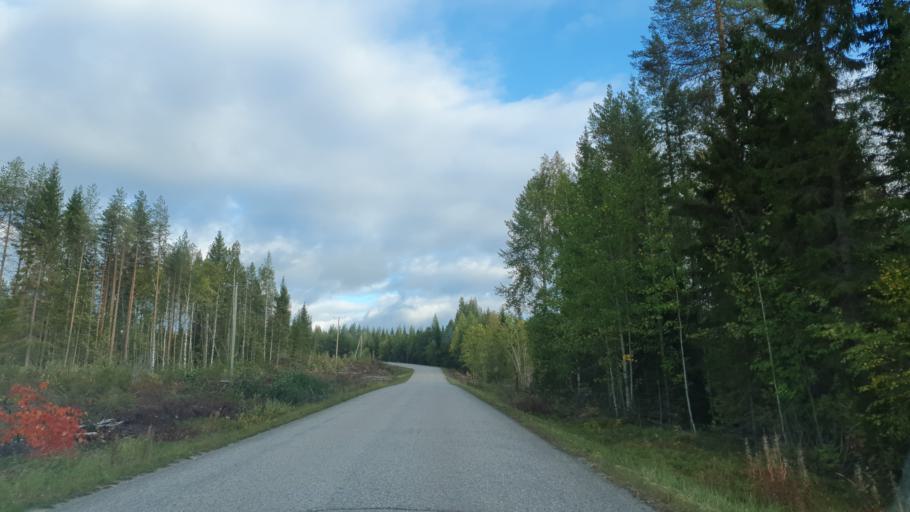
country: FI
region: Kainuu
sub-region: Kehys-Kainuu
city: Kuhmo
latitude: 63.9258
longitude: 30.0116
